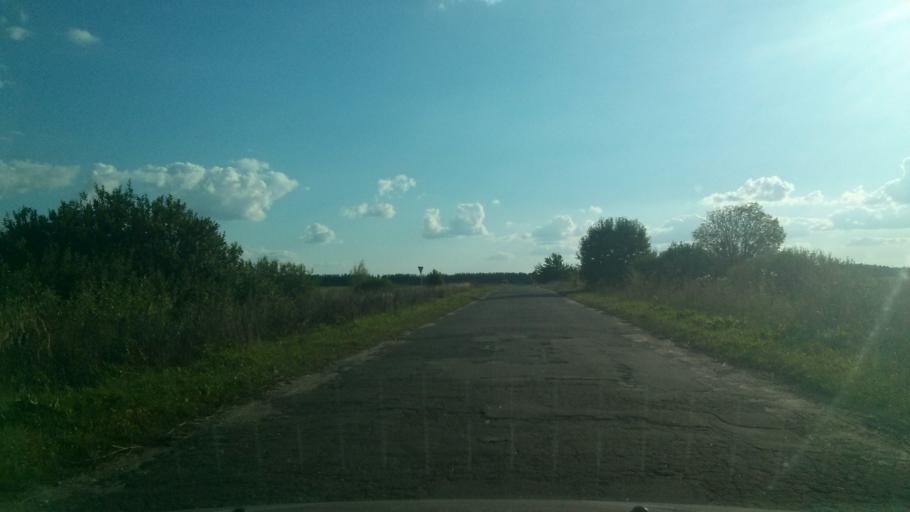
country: RU
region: Nizjnij Novgorod
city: Shimorskoye
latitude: 55.3025
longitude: 41.8362
